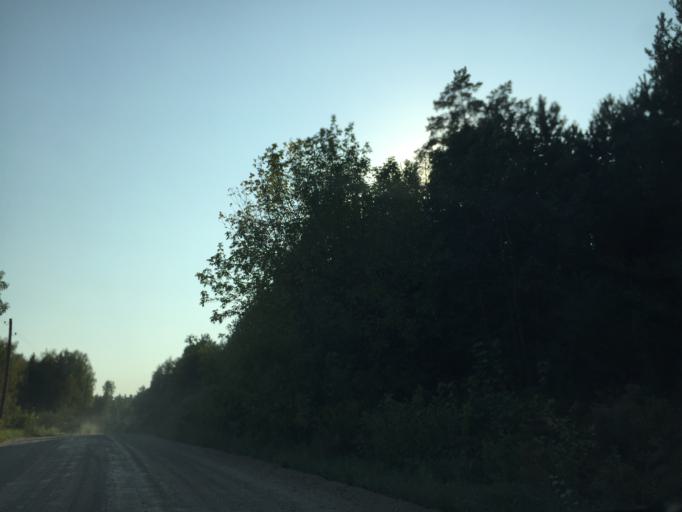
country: LV
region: Ogre
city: Ogre
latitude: 56.8394
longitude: 24.5829
